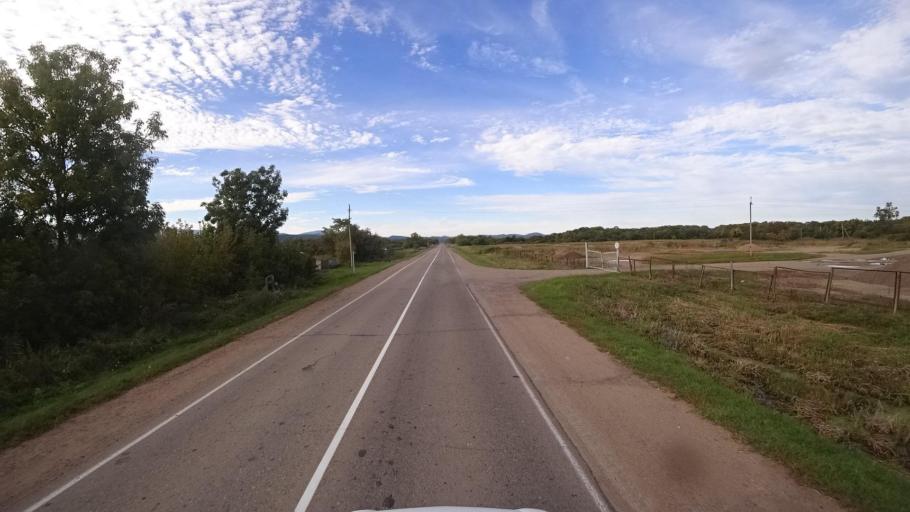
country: RU
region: Primorskiy
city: Dostoyevka
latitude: 44.2979
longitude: 133.4263
